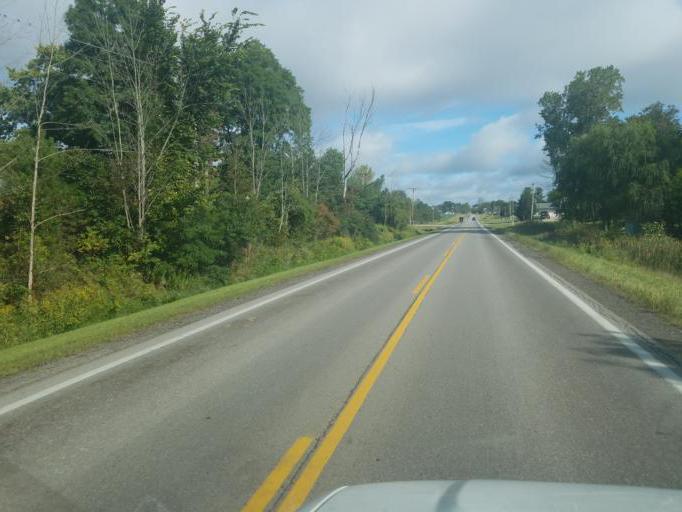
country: US
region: Ohio
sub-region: Wayne County
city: West Salem
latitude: 40.9599
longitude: -82.1095
